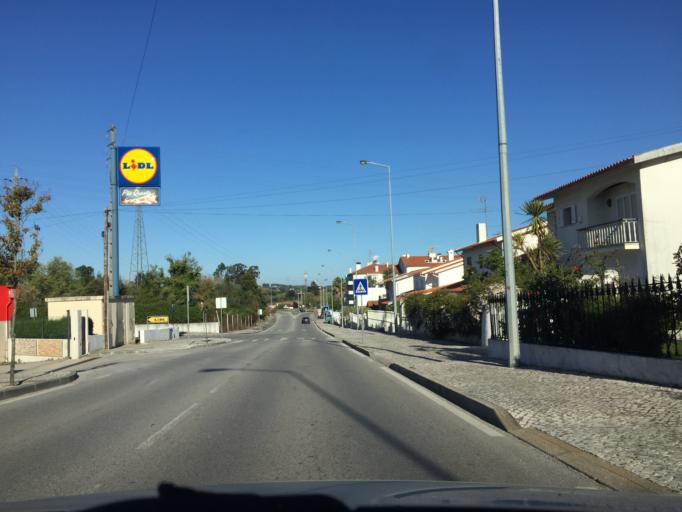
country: PT
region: Aveiro
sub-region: Anadia
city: Arcos
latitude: 40.4426
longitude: -8.4493
